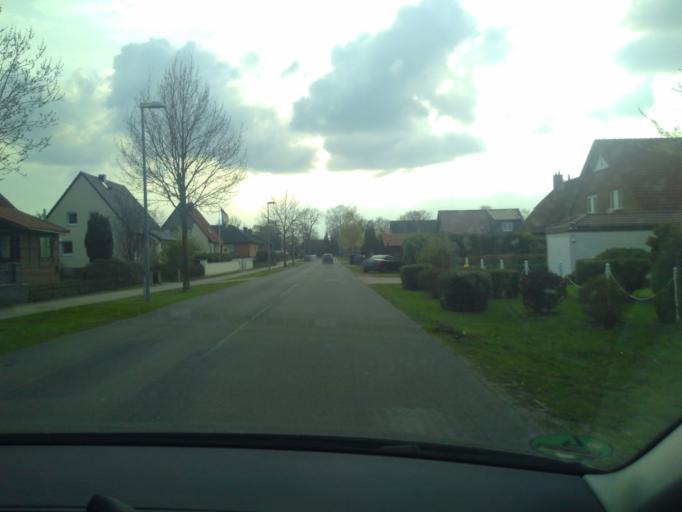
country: DE
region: Lower Saxony
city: Adelheidsdorf
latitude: 52.5515
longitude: 10.0198
